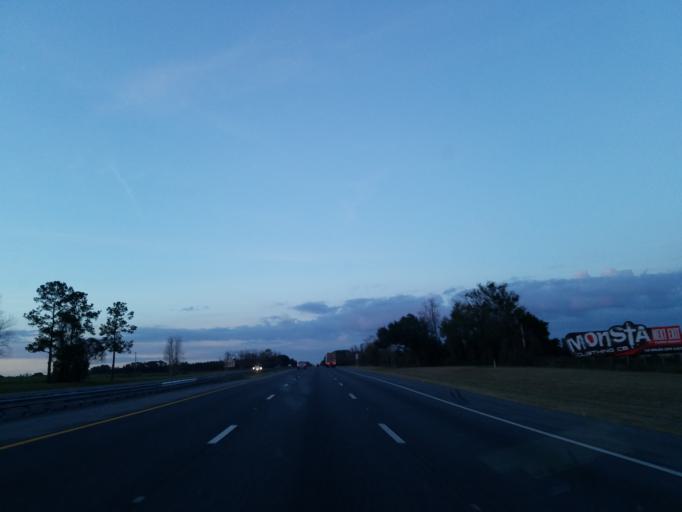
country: US
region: Florida
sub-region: Alachua County
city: High Springs
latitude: 30.0051
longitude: -82.6034
